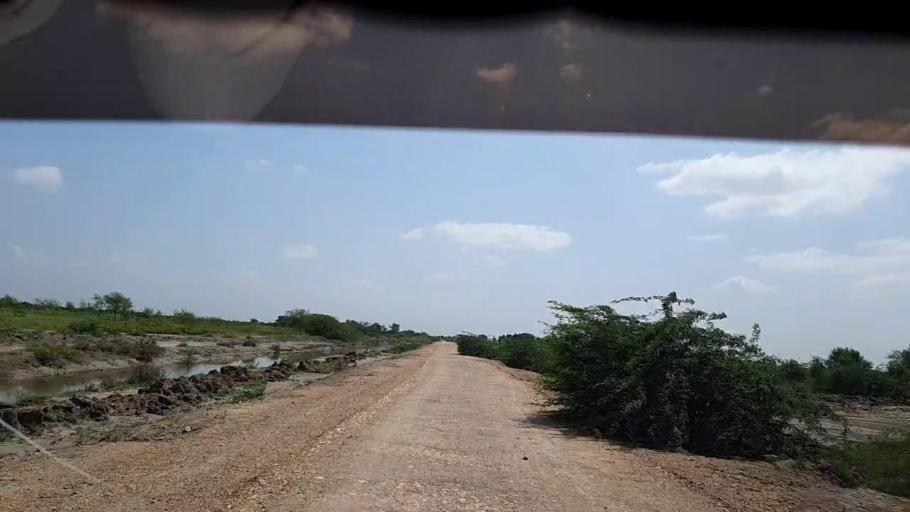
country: PK
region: Sindh
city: Kadhan
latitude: 24.5951
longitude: 68.9918
